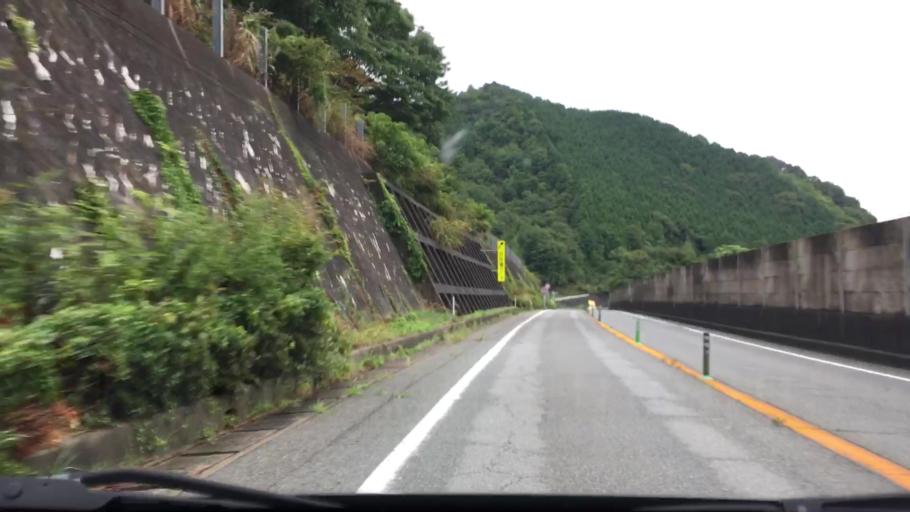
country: JP
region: Hyogo
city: Nishiwaki
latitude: 35.0369
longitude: 134.7699
